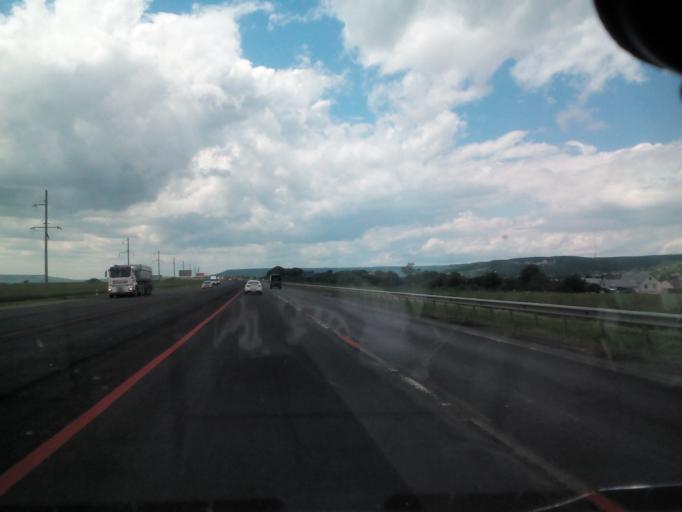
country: RU
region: Stavropol'skiy
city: Tatarka
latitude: 44.9533
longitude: 41.9756
